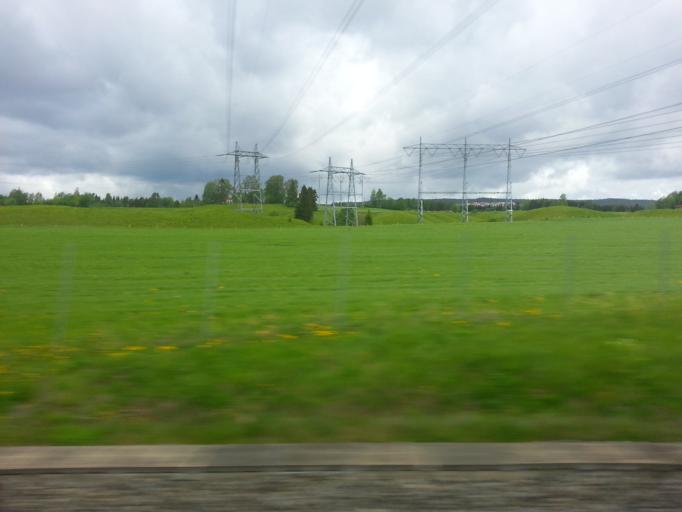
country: NO
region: Akershus
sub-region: Skedsmo
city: Leirsund
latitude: 59.9959
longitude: 11.0824
